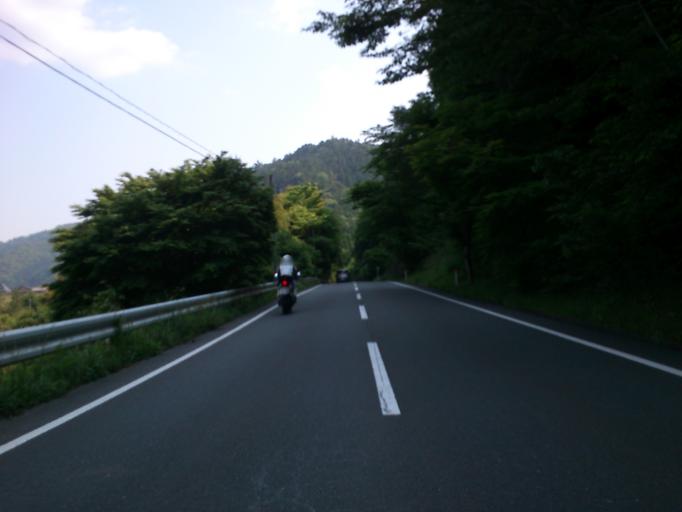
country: JP
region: Kyoto
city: Kameoka
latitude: 35.2436
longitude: 135.5586
